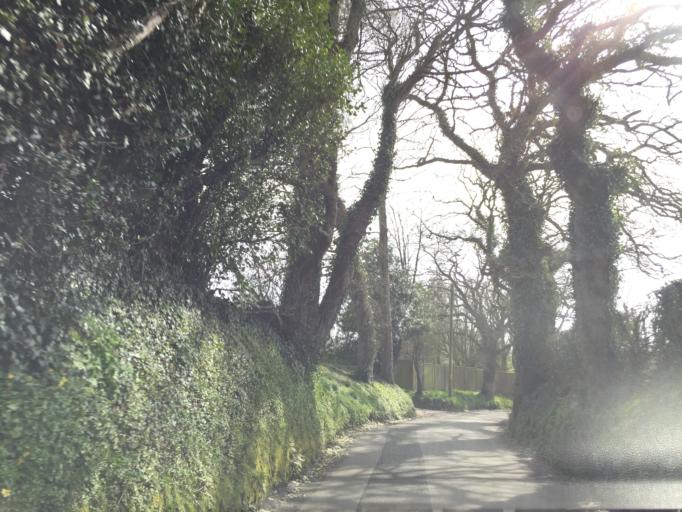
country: JE
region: St Helier
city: Saint Helier
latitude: 49.2038
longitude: -2.0696
